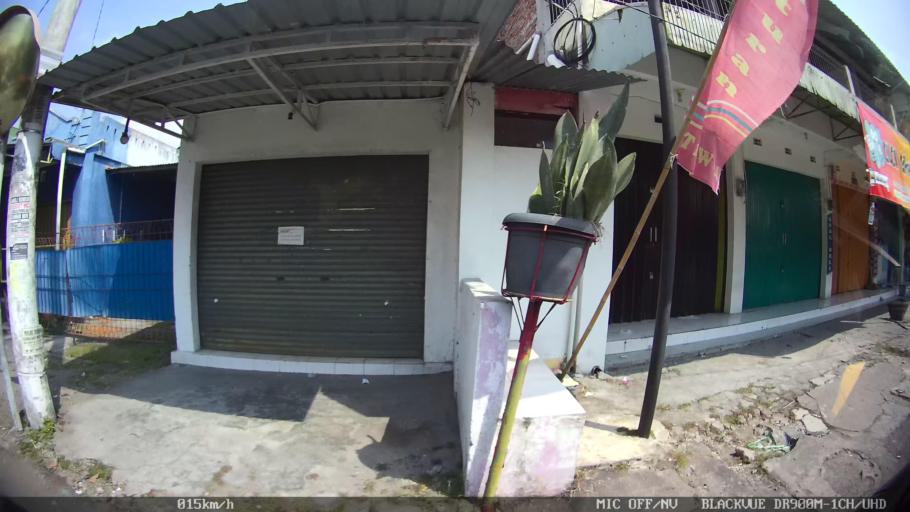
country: ID
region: Daerah Istimewa Yogyakarta
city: Yogyakarta
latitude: -7.8067
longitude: 110.3900
